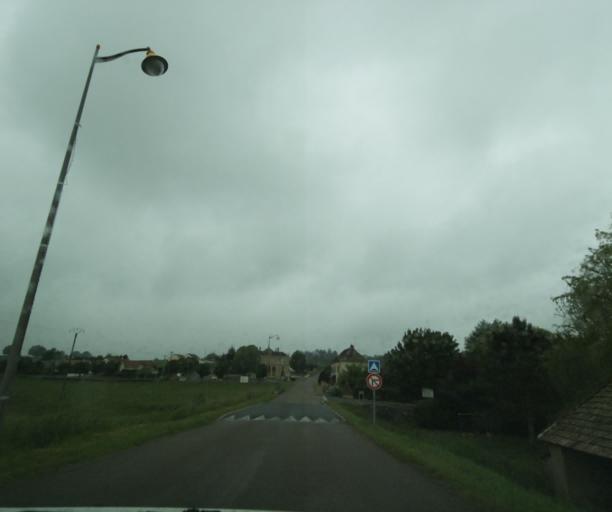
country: FR
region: Bourgogne
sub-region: Departement de Saone-et-Loire
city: Palinges
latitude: 46.4964
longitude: 4.2139
